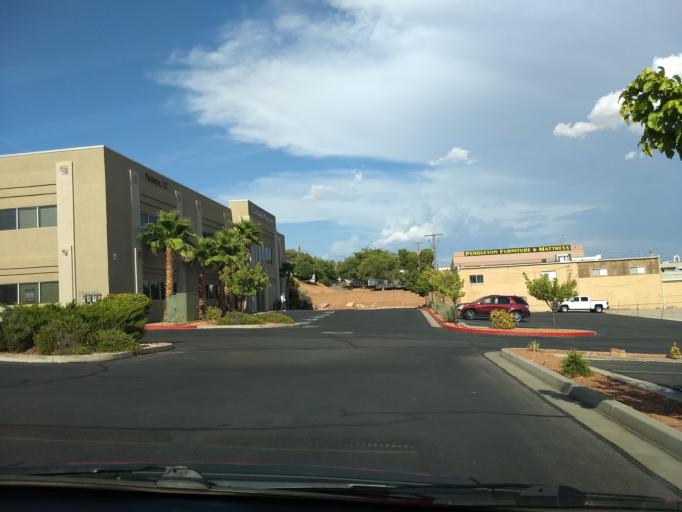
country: US
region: Utah
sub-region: Washington County
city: Saint George
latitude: 37.1107
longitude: -113.5738
